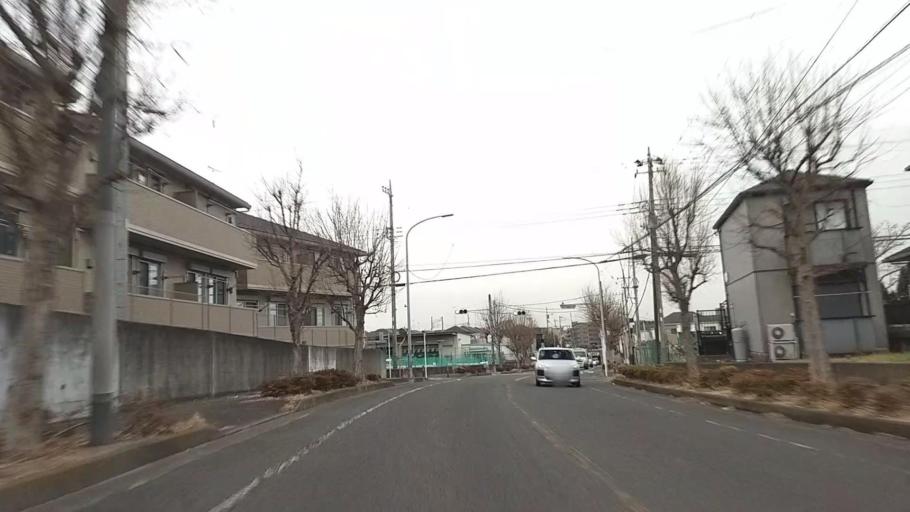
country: JP
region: Tokyo
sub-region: Machida-shi
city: Machida
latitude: 35.5168
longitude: 139.4572
